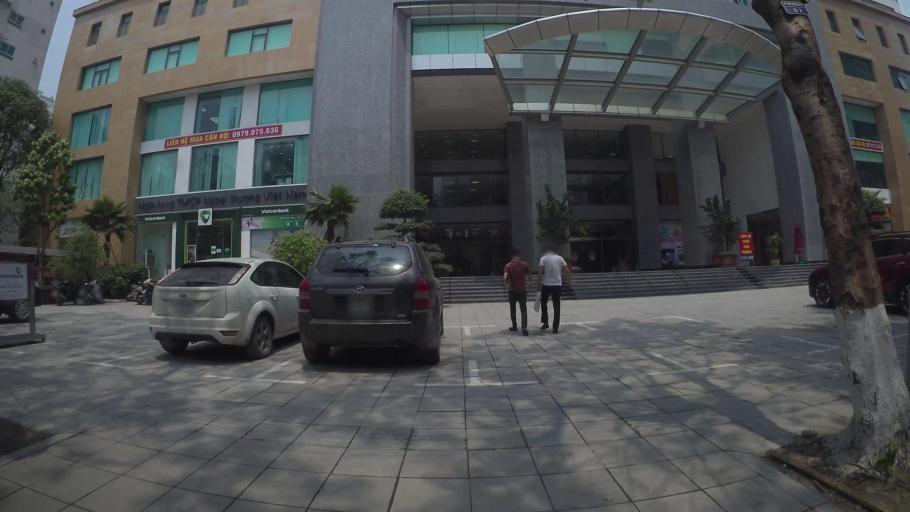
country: VN
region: Ha Noi
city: Thanh Xuan
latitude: 20.9992
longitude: 105.8008
